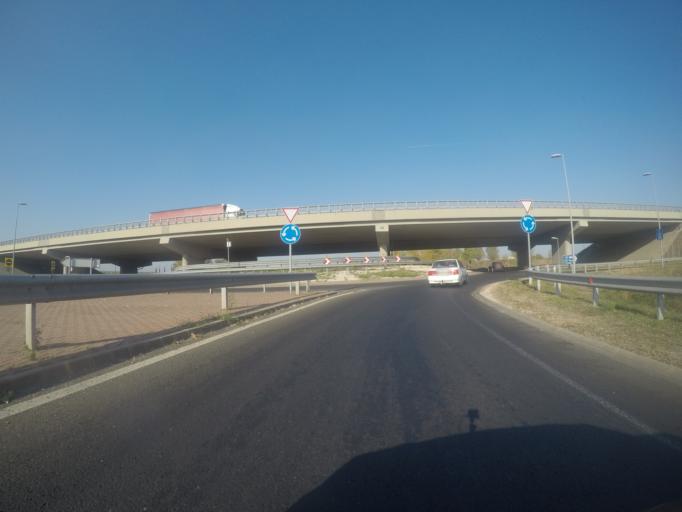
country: HU
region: Fejer
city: Baracs
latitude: 46.9102
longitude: 18.9261
